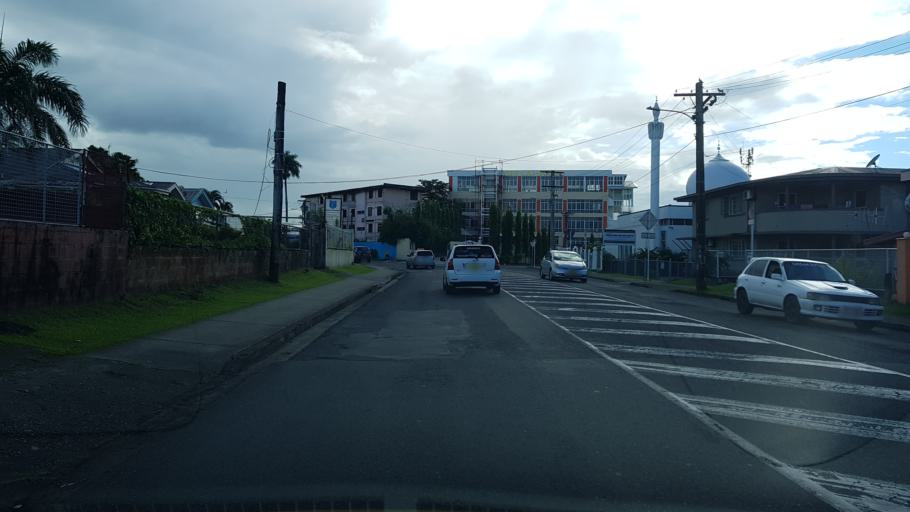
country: FJ
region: Central
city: Suva
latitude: -18.1459
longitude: 178.4325
